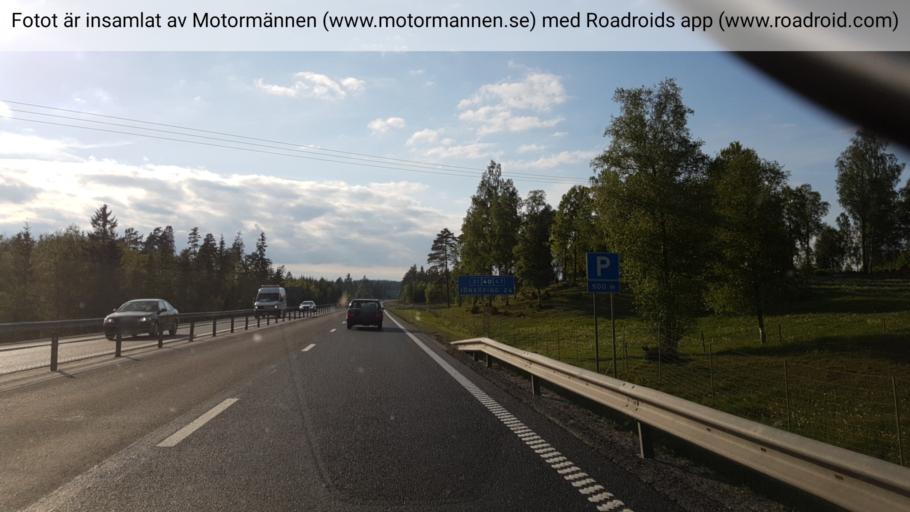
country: SE
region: Joenkoeping
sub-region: Nassjo Kommun
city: Malmback
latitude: 57.6878
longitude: 14.4595
